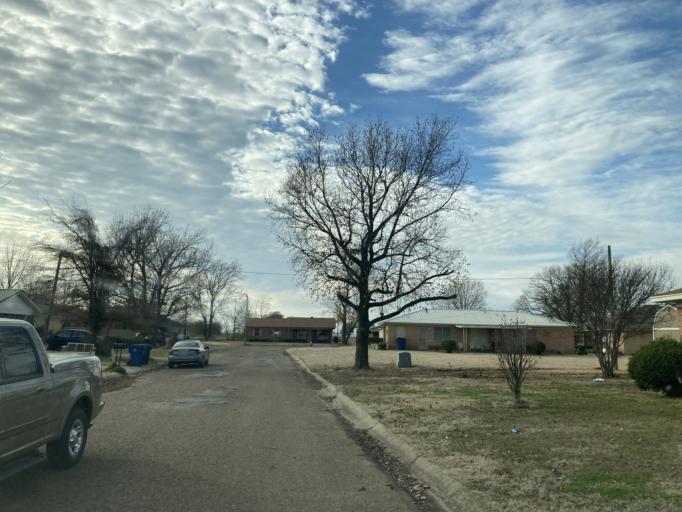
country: US
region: Mississippi
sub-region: Humphreys County
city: Belzoni
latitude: 33.1682
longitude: -90.5025
